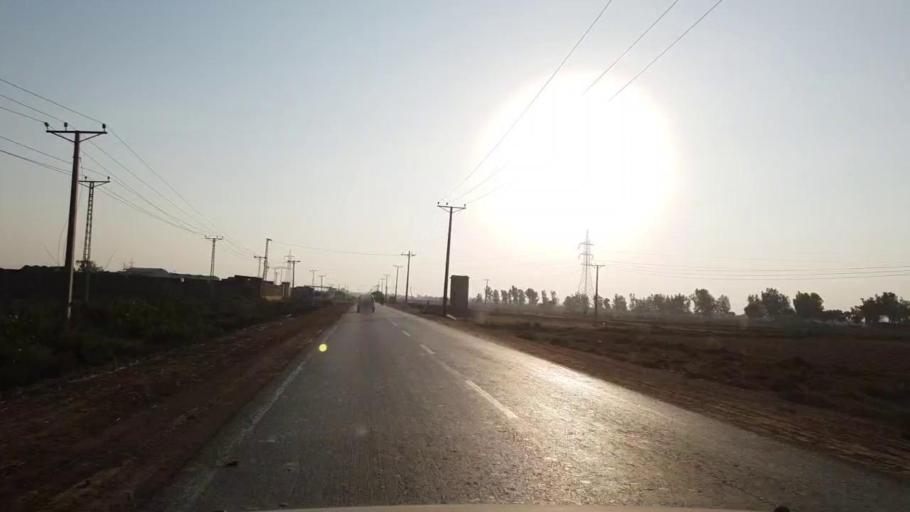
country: PK
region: Sindh
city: Daro Mehar
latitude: 24.6187
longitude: 68.0936
